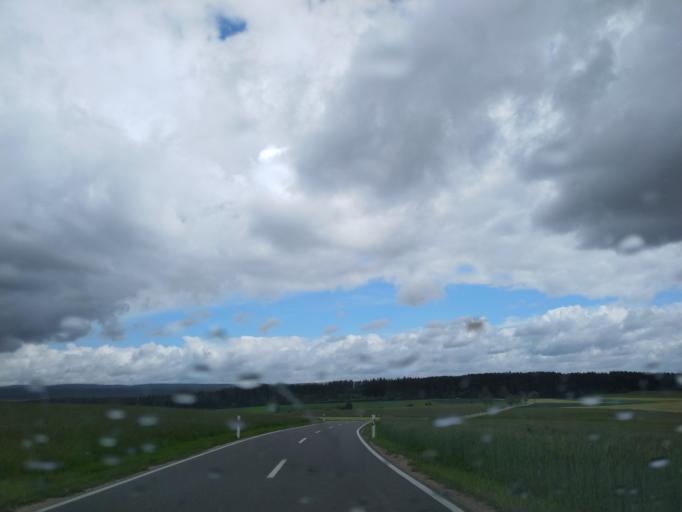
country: DE
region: Baden-Wuerttemberg
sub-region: Freiburg Region
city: Loffingen
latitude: 47.8660
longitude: 8.3093
